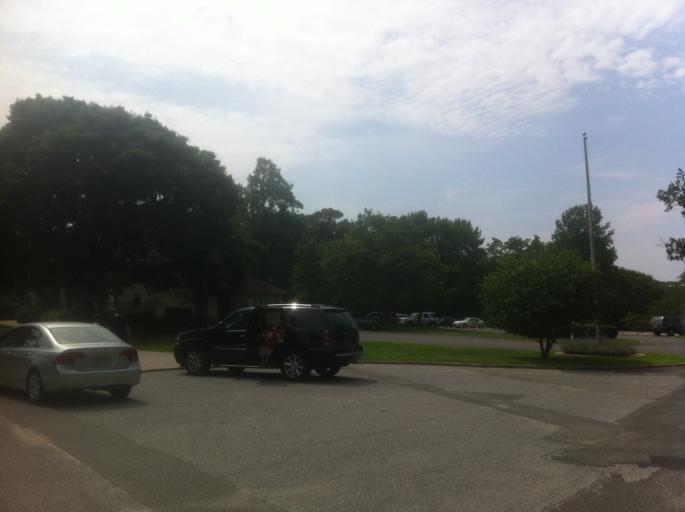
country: US
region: New York
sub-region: Nassau County
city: Locust Valley
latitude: 40.8726
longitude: -73.5742
